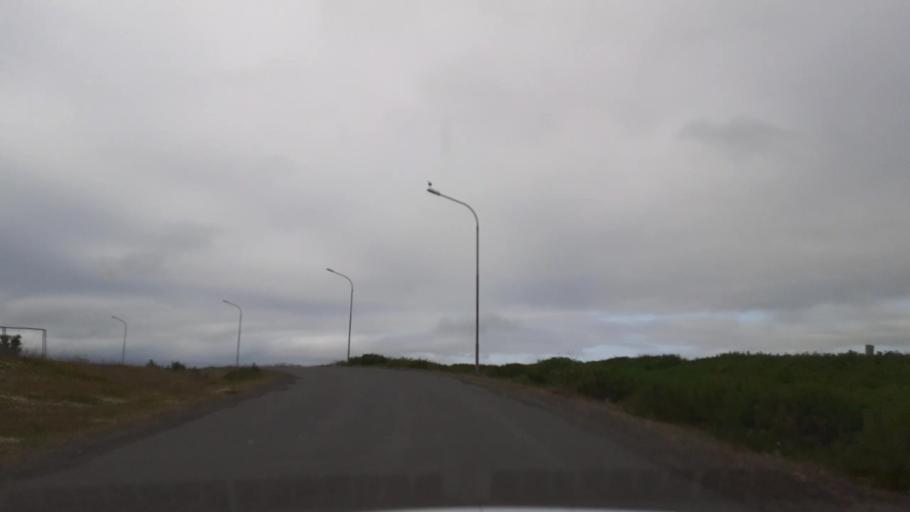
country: IS
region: Northwest
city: Saudarkrokur
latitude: 65.9001
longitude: -19.4159
